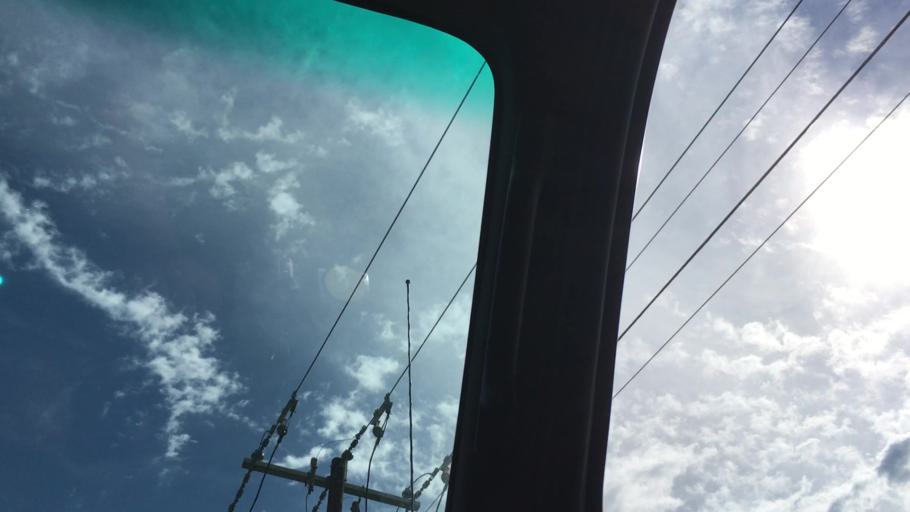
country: US
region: Maryland
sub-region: Worcester County
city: Pocomoke City
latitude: 38.0609
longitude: -75.5505
